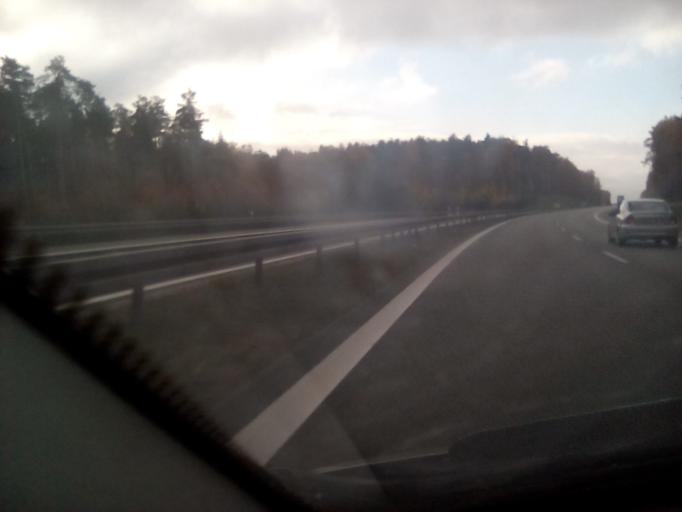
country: PL
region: Masovian Voivodeship
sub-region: Powiat bialobrzeski
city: Bialobrzegi
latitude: 51.6440
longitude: 20.9745
